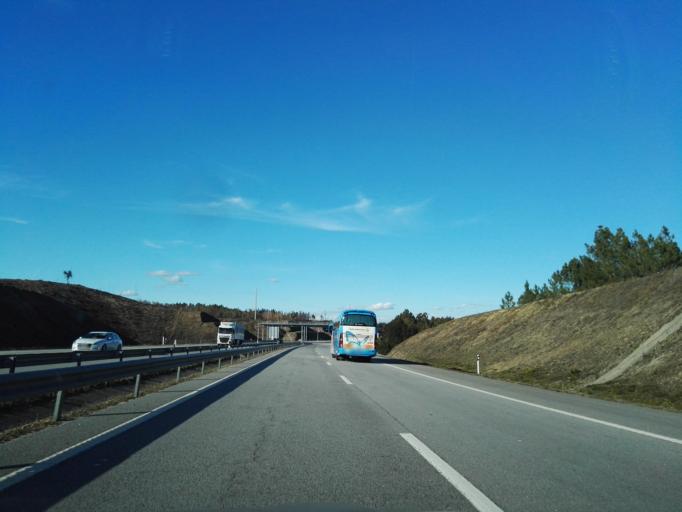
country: PT
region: Portalegre
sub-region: Nisa
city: Nisa
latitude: 39.7016
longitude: -7.6954
